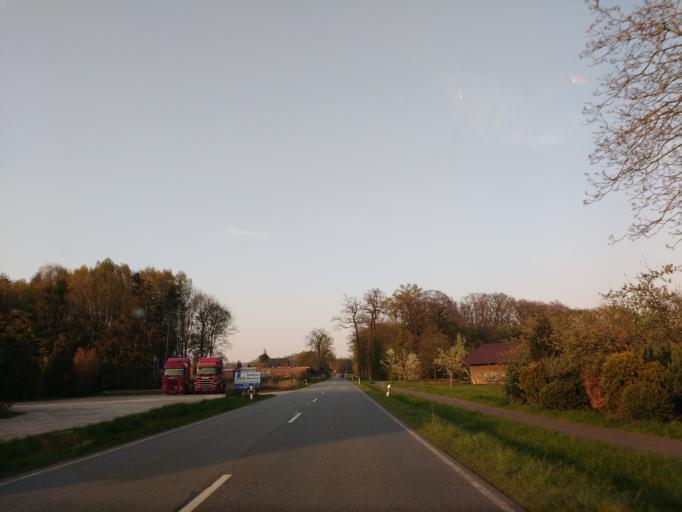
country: DE
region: Lower Saxony
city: Dissen
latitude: 52.0720
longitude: 8.2312
